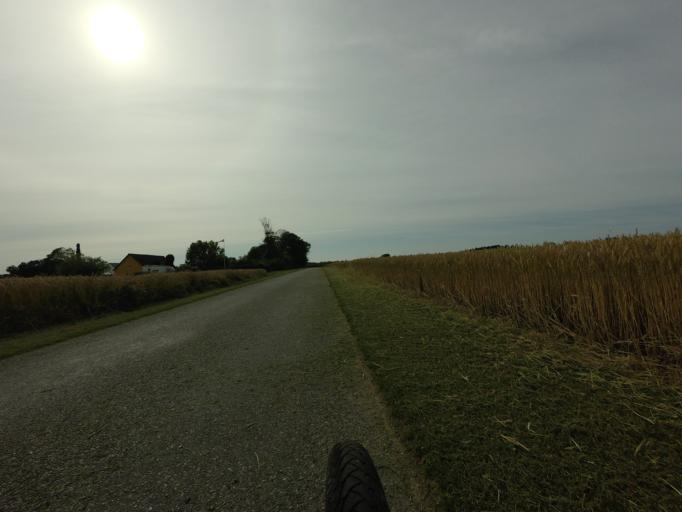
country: DK
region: North Denmark
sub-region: Hjorring Kommune
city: Hjorring
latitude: 57.4407
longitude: 9.8607
